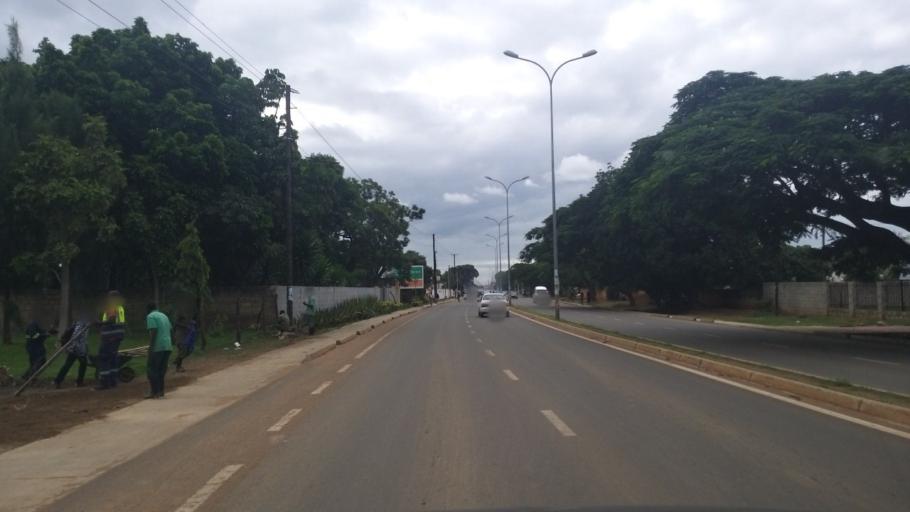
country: ZM
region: Lusaka
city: Lusaka
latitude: -15.4364
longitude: 28.3108
